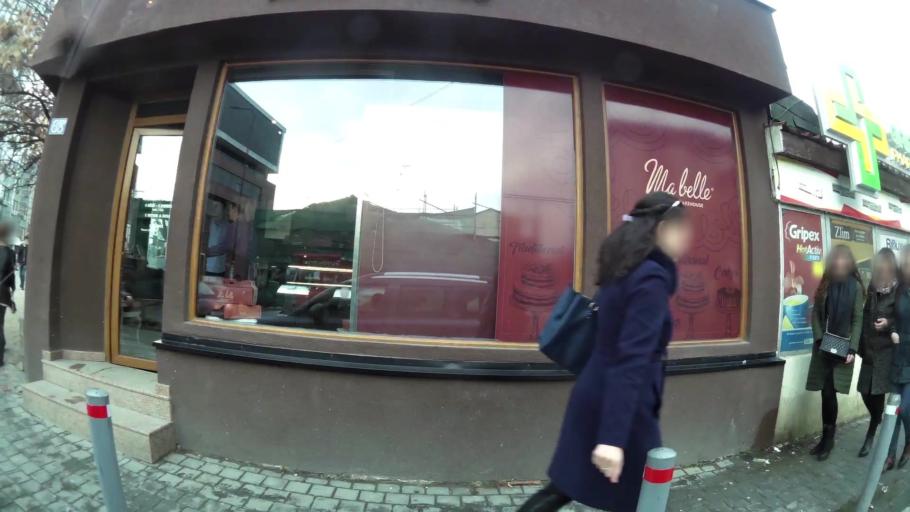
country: XK
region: Pristina
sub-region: Komuna e Prishtines
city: Pristina
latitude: 42.6638
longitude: 21.1609
